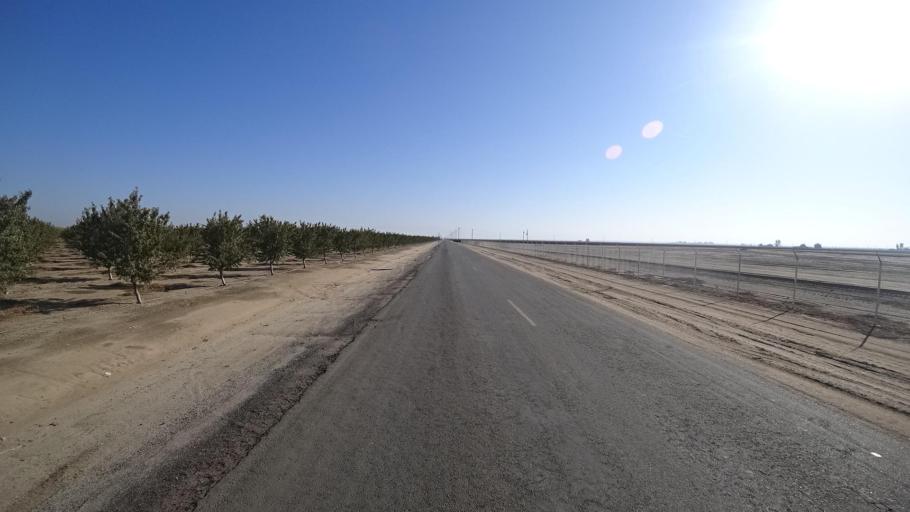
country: US
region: California
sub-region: Kern County
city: Delano
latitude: 35.7687
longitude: -119.2131
